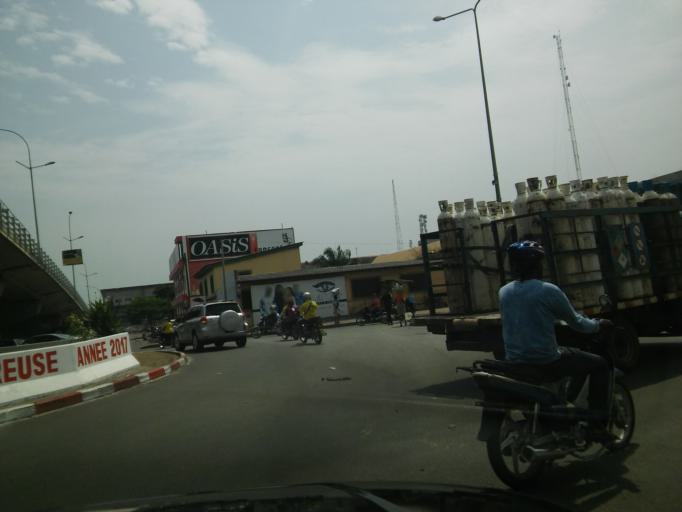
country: BJ
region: Littoral
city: Cotonou
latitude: 6.3575
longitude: 2.4374
